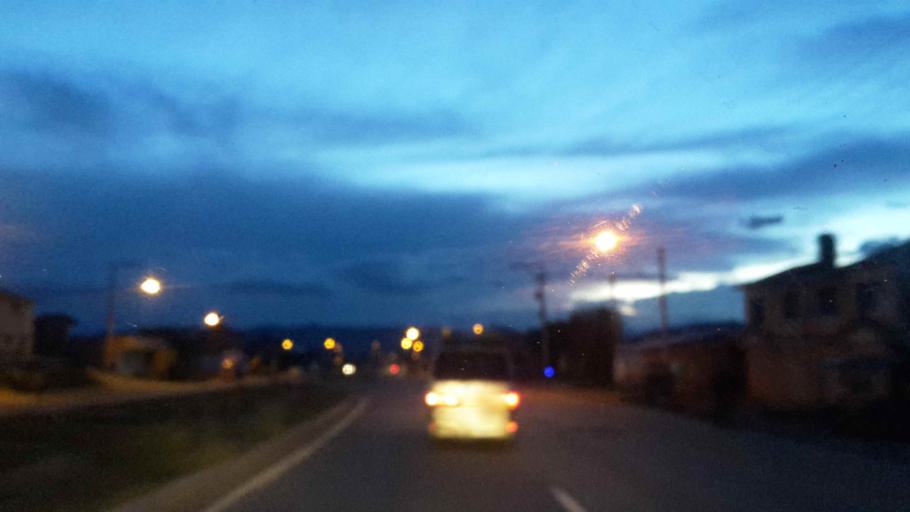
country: BO
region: Cochabamba
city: Colomi
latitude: -17.4051
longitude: -65.9805
